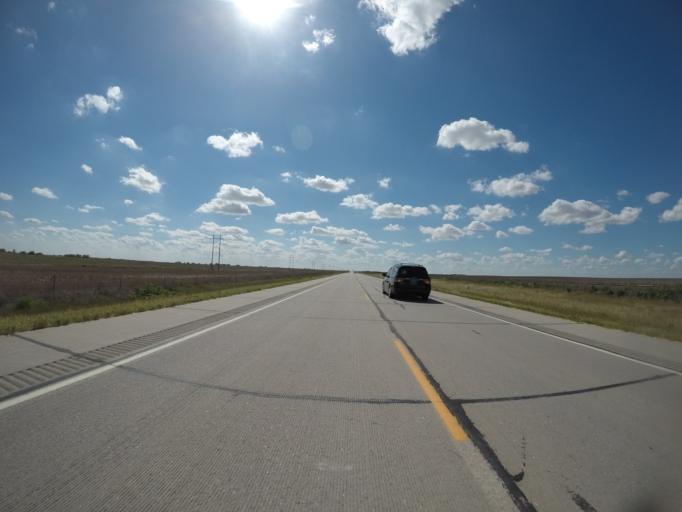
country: US
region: Colorado
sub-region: Phillips County
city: Holyoke
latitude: 40.5950
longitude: -102.3687
